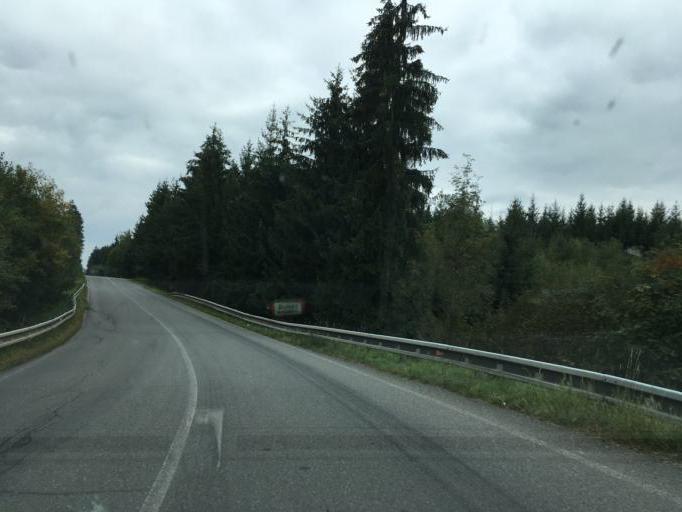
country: CZ
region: Vysocina
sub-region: Okres Pelhrimov
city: Zeliv
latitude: 49.5499
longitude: 15.1419
